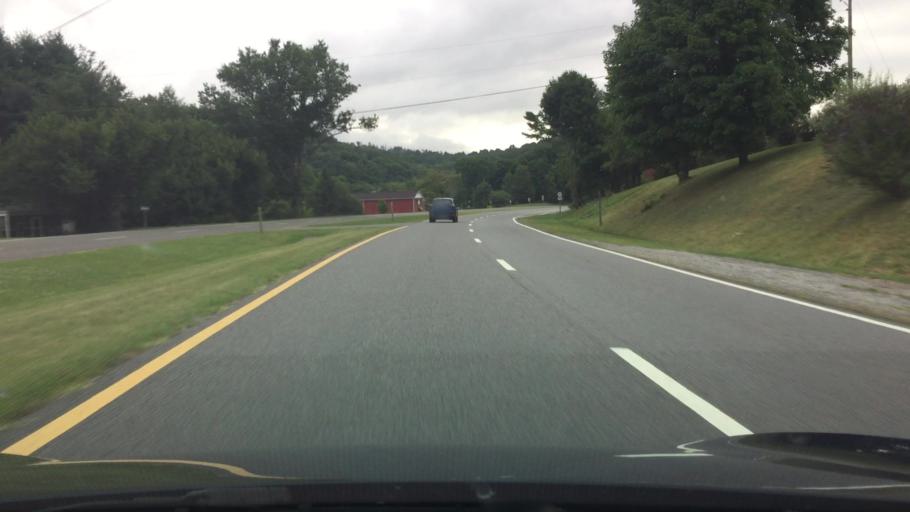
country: US
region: Virginia
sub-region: Montgomery County
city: Shawsville
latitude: 37.2184
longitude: -80.2303
